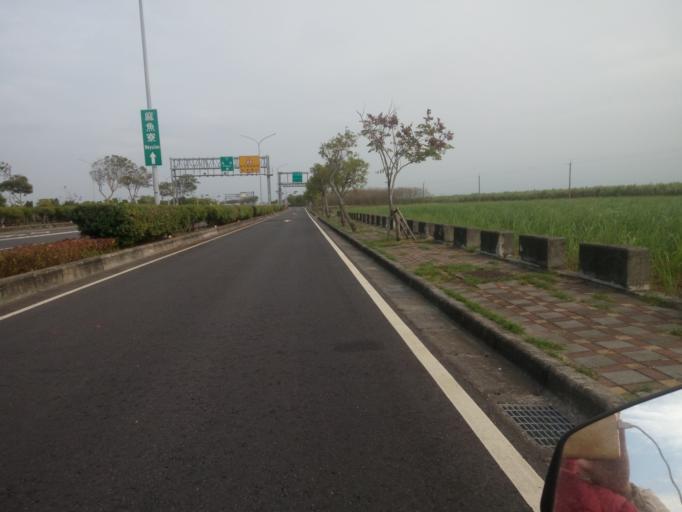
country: TW
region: Taiwan
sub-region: Chiayi
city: Taibao
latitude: 23.4828
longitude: 120.3675
